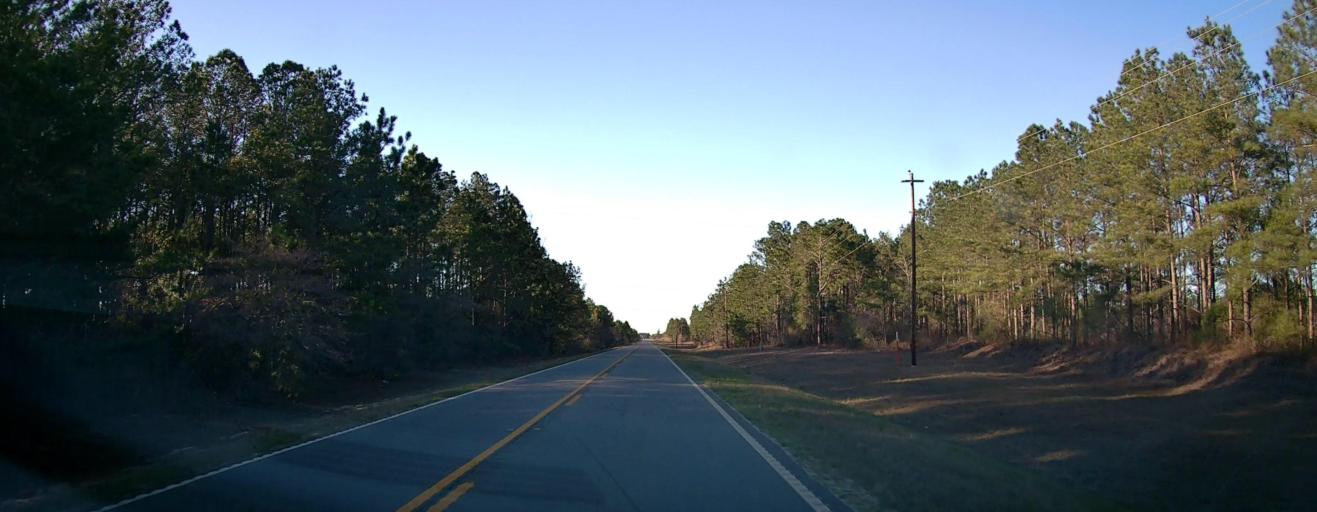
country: US
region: Georgia
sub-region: Talbot County
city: Talbotton
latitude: 32.5742
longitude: -84.4428
